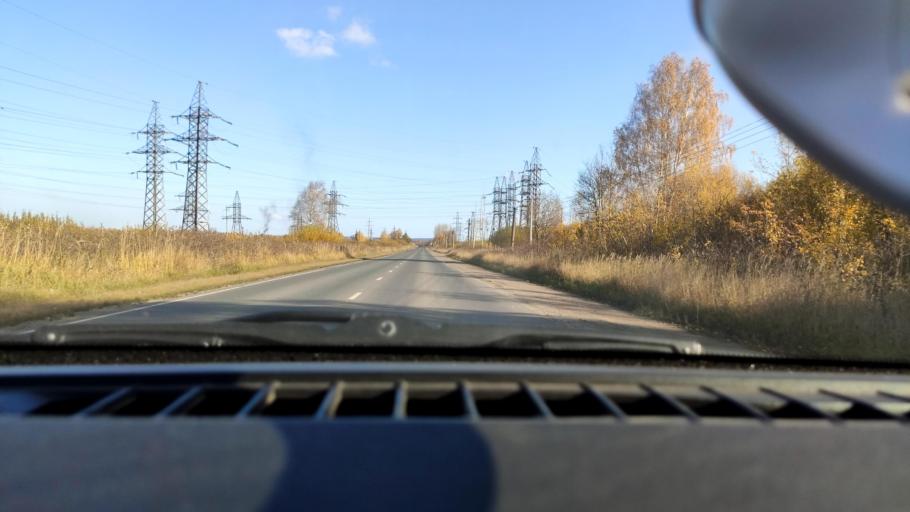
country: RU
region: Perm
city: Gamovo
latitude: 57.8883
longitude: 56.1704
